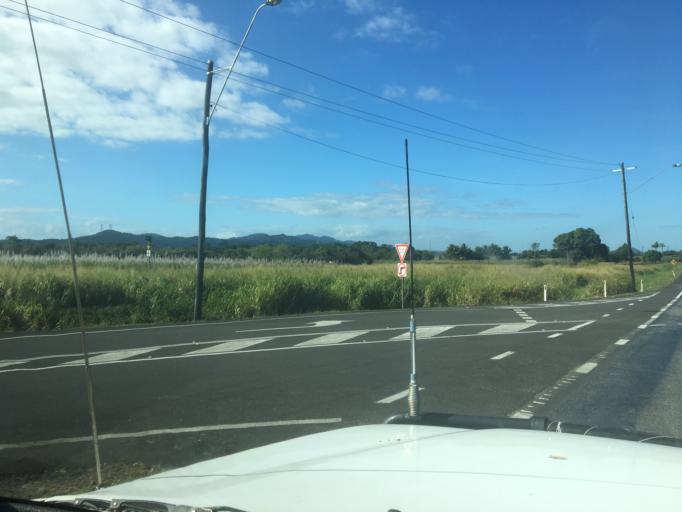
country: AU
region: Queensland
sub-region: Cassowary Coast
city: Innisfail
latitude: -17.3225
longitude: 145.9282
